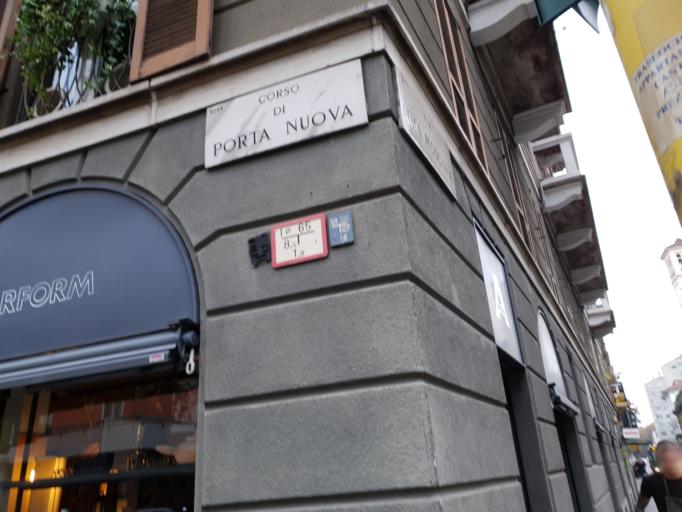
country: IT
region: Lombardy
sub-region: Citta metropolitana di Milano
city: Milano
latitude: 45.4764
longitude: 9.1919
